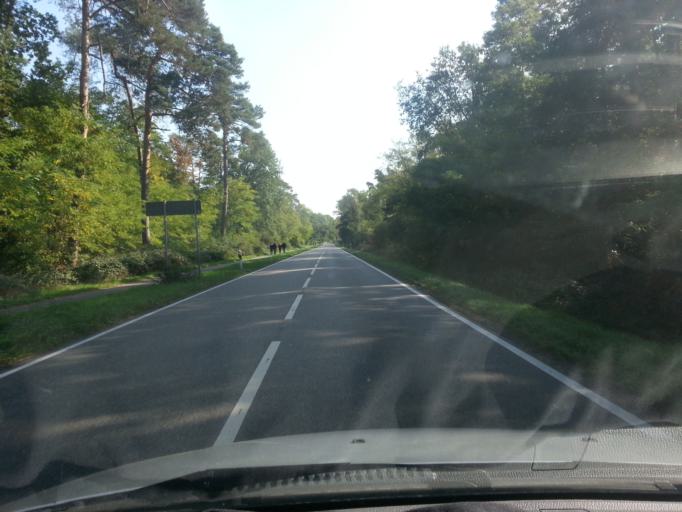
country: DE
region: Rheinland-Pfalz
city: Schifferstadt
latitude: 49.3660
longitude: 8.3940
